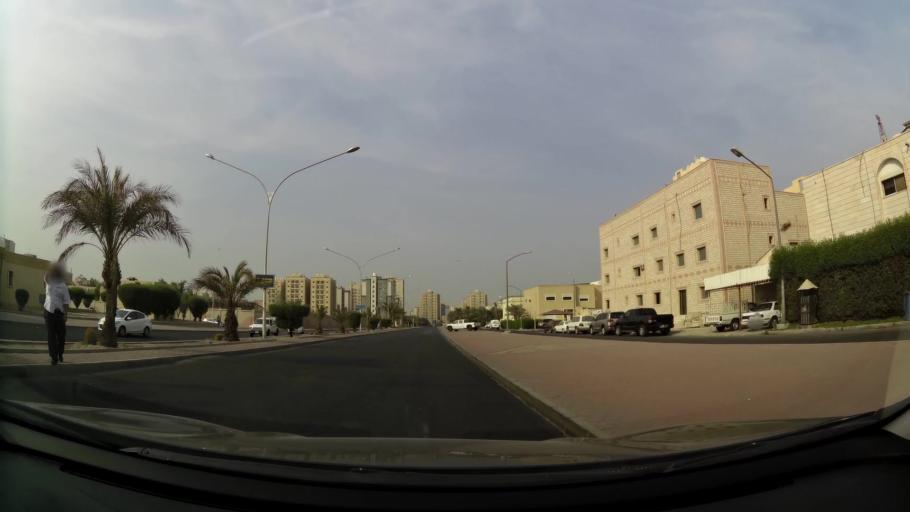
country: KW
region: Al Farwaniyah
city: Janub as Surrah
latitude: 29.2780
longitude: 47.9777
